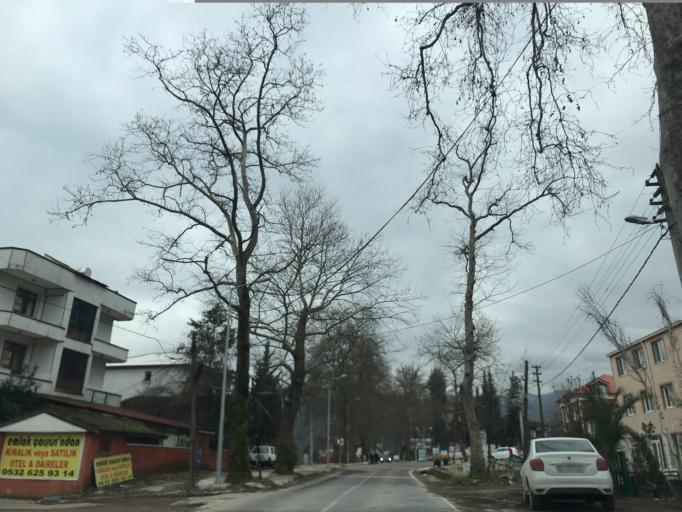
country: TR
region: Yalova
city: Kadikoy
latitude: 40.6115
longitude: 29.2111
